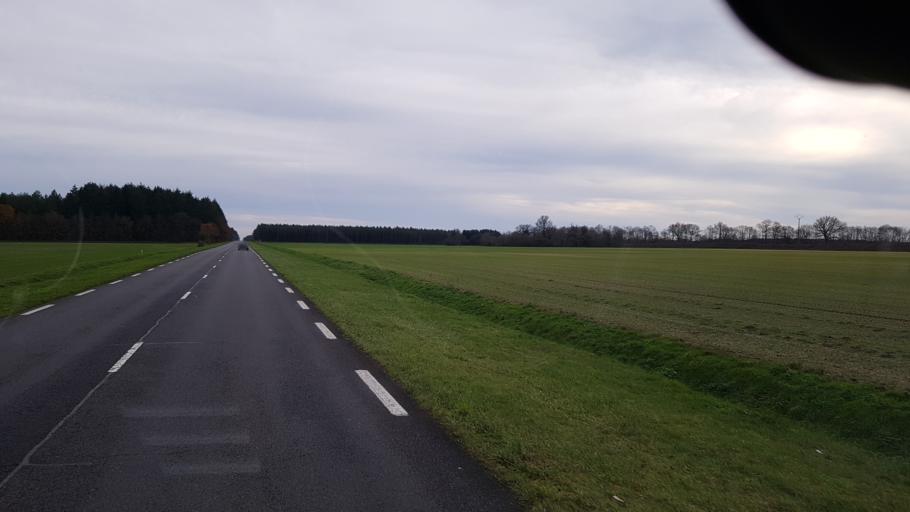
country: FR
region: Centre
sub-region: Departement du Loir-et-Cher
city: Lamotte-Beuvron
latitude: 47.6413
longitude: 1.9964
